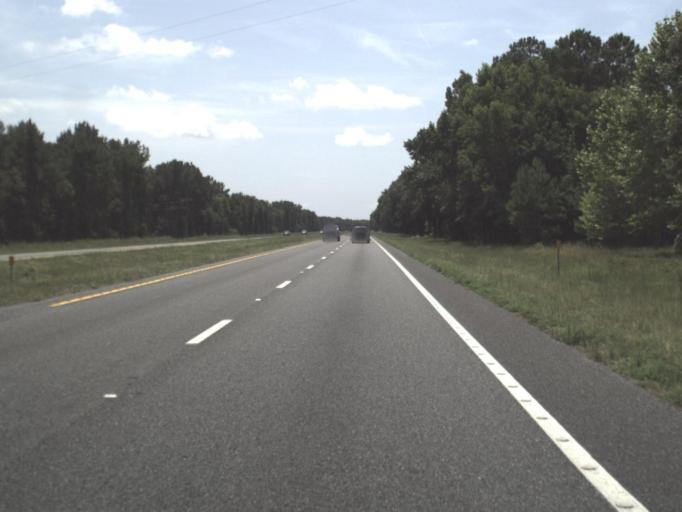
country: US
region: Florida
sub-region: Taylor County
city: Perry
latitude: 30.0025
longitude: -83.5102
